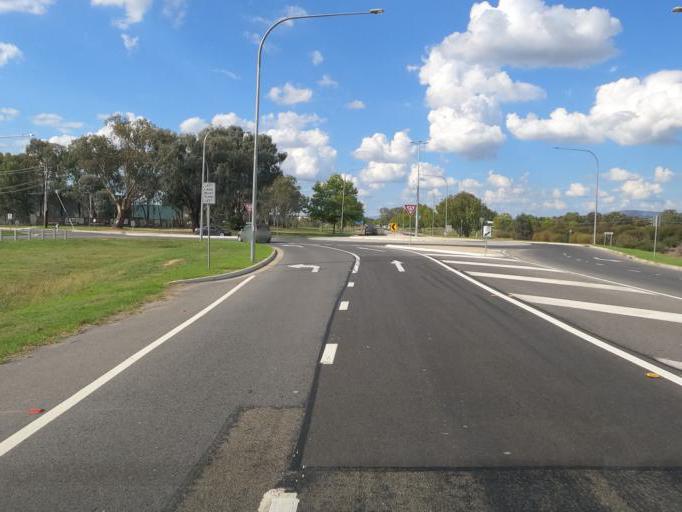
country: AU
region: New South Wales
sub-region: Albury Municipality
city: East Albury
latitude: -36.0761
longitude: 146.9471
